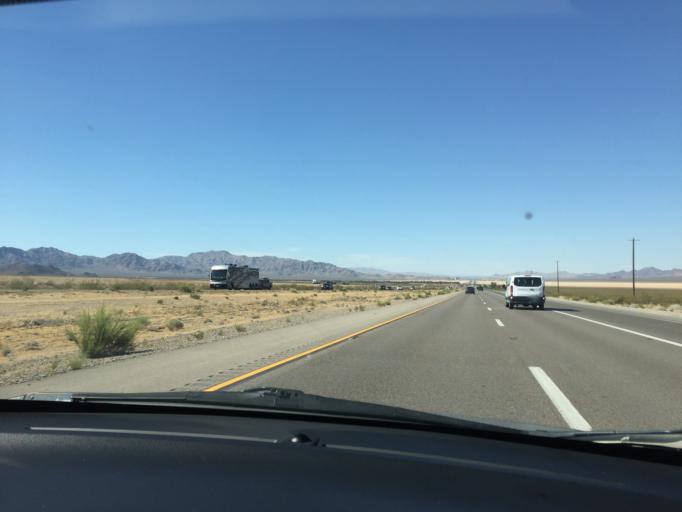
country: US
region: Nevada
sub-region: Clark County
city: Sandy Valley
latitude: 35.5160
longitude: -115.4302
